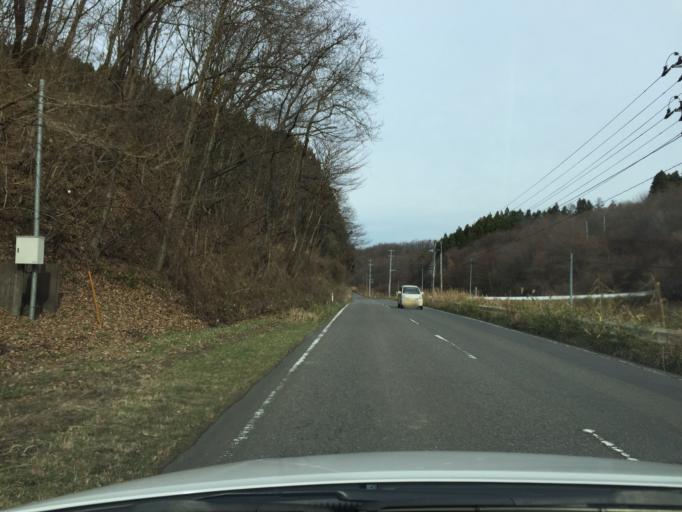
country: JP
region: Fukushima
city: Ishikawa
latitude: 37.2273
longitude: 140.6289
